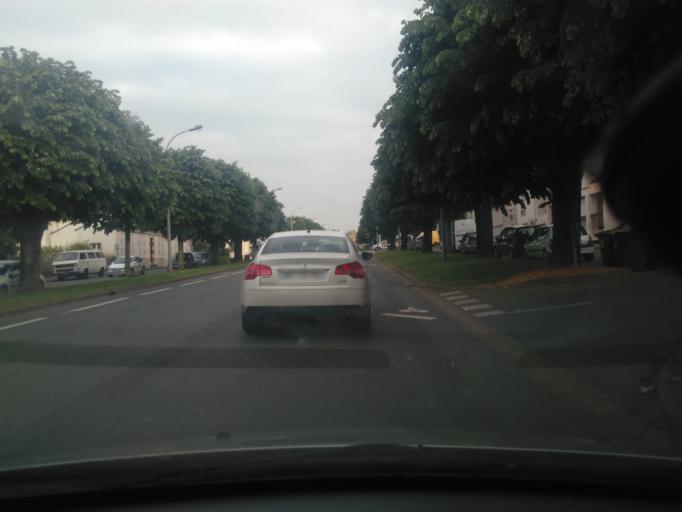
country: FR
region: Pays de la Loire
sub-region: Departement de la Vendee
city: La Roche-sur-Yon
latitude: 46.6740
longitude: -1.4214
